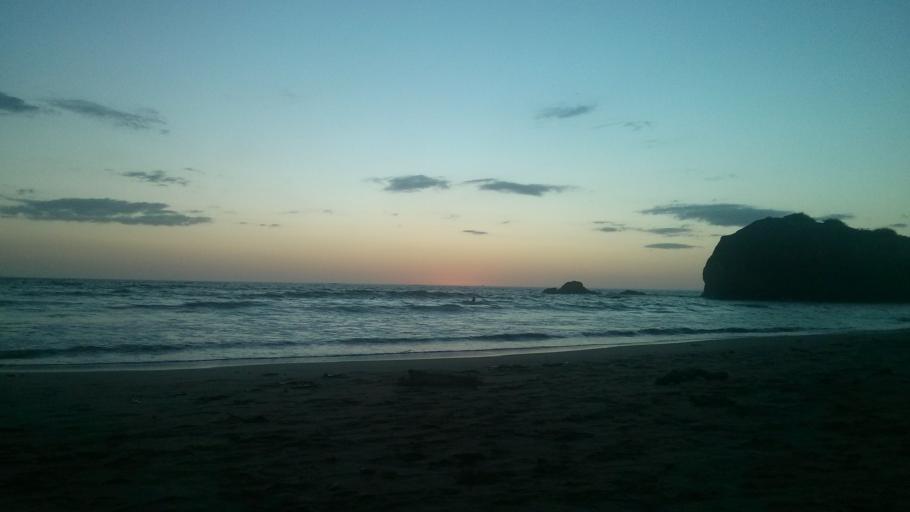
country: CR
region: Guanacaste
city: Sardinal
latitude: 10.3387
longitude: -85.8526
